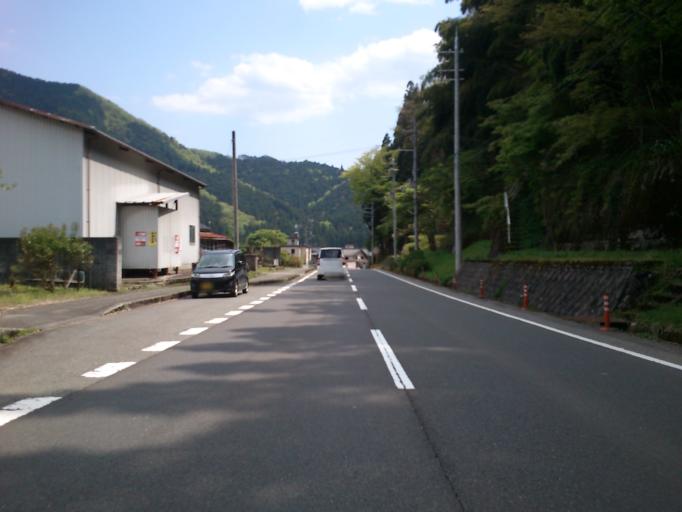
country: JP
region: Kyoto
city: Fukuchiyama
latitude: 35.3520
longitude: 134.9443
